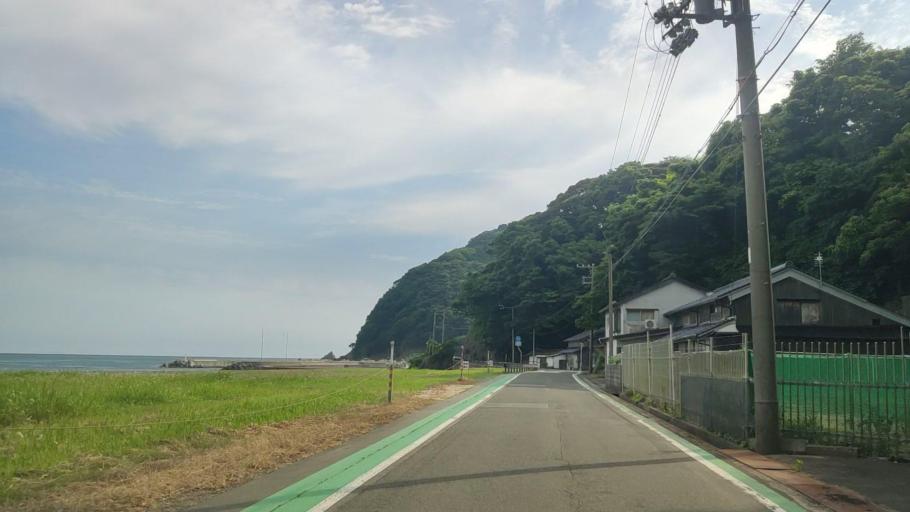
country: JP
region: Hyogo
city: Toyooka
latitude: 35.6420
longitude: 134.8421
